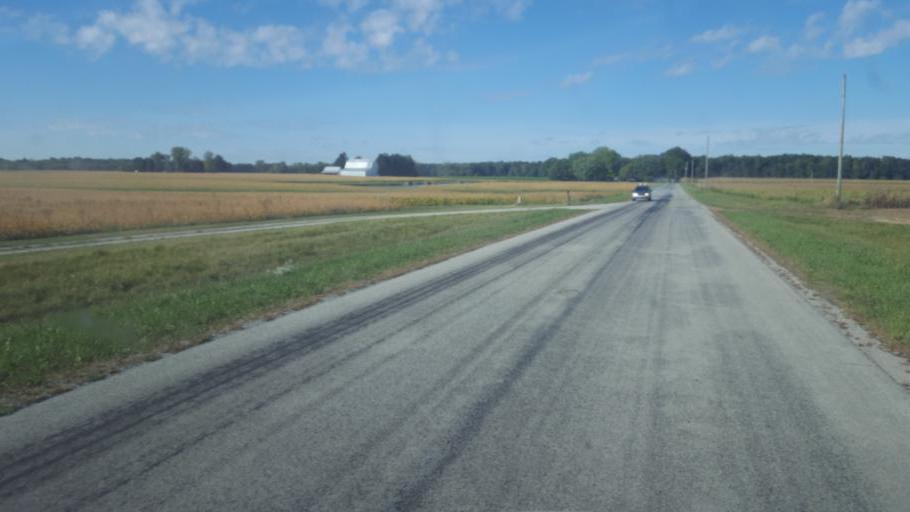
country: US
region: Ohio
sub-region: Wyandot County
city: Upper Sandusky
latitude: 40.8036
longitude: -83.2406
